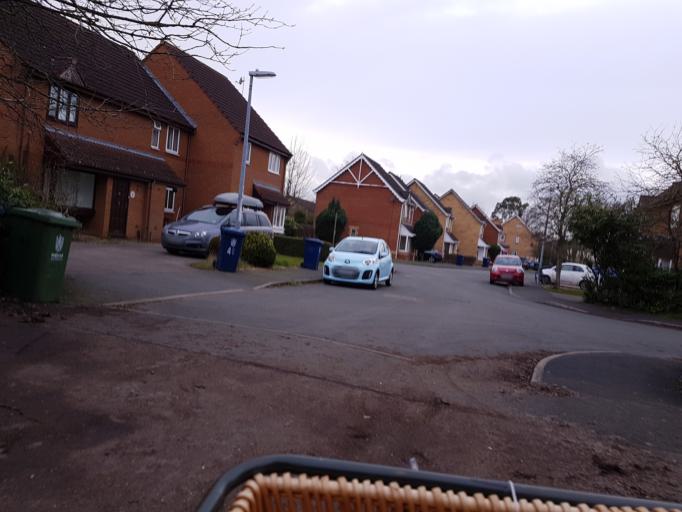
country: GB
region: England
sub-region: Cambridgeshire
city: Fulbourn
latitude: 52.1874
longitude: 0.1832
